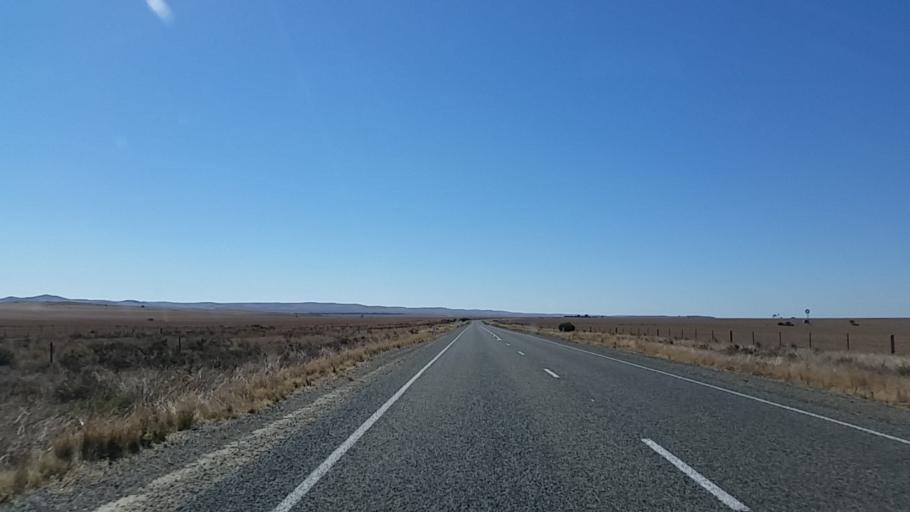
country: AU
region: South Australia
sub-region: Northern Areas
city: Jamestown
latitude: -33.2772
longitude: 138.8686
